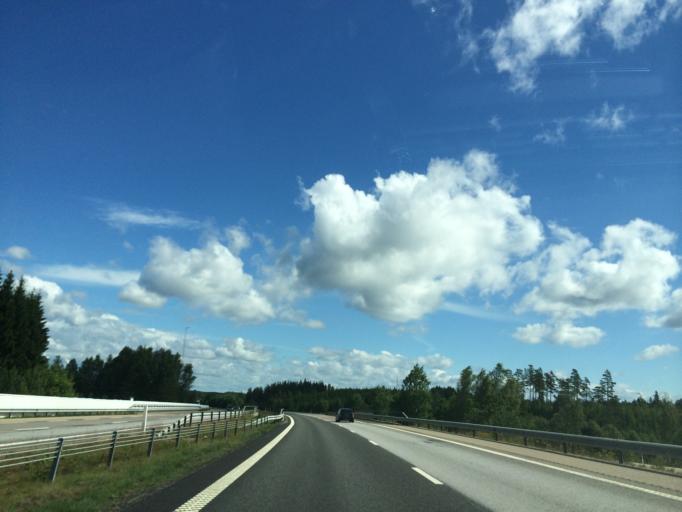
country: SE
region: Kronoberg
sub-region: Markaryds Kommun
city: Stromsnasbruk
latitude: 56.6218
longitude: 13.7823
